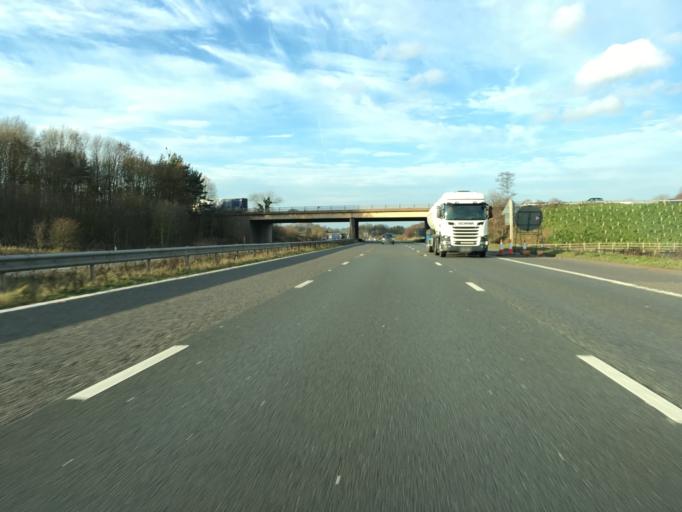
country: GB
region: England
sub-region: Trafford
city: Bowdon
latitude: 53.3634
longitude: -2.3897
